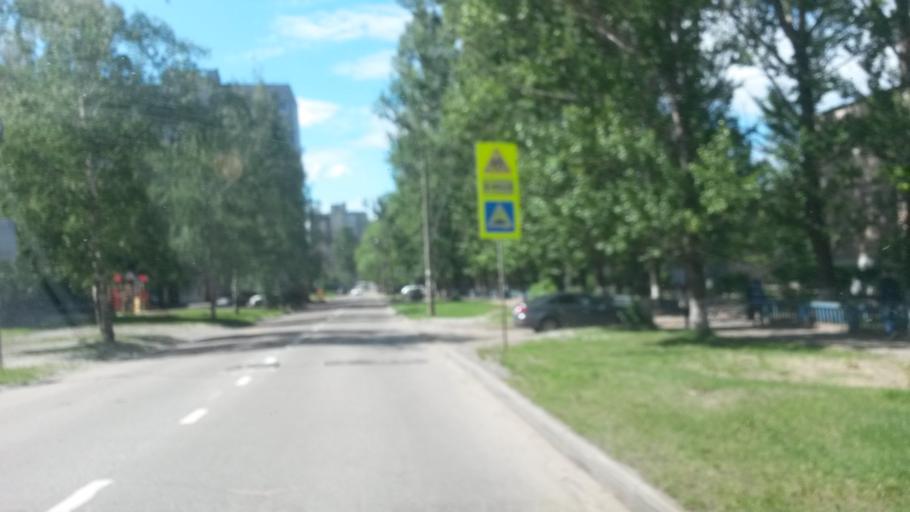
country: RU
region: Jaroslavl
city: Yaroslavl
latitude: 57.5831
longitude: 39.8289
